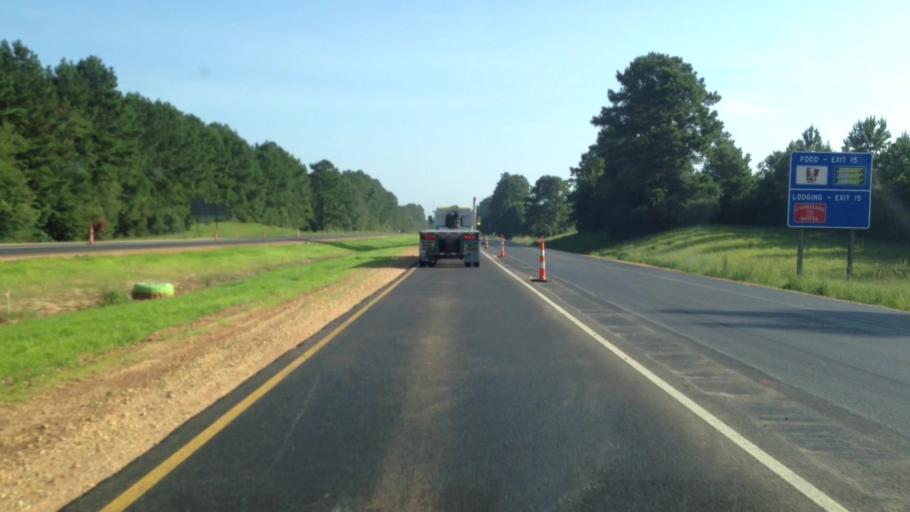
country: US
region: Mississippi
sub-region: Pike County
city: McComb
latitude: 31.2062
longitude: -90.4838
